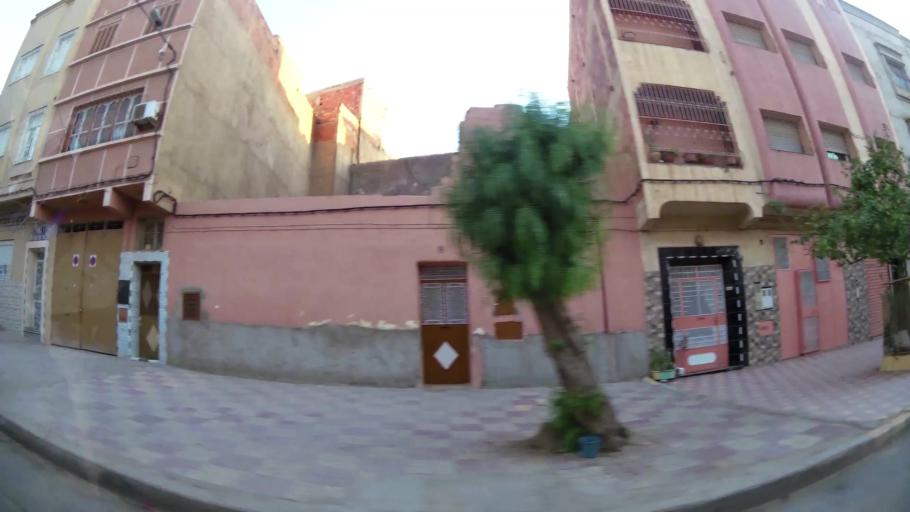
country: MA
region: Oriental
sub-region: Berkane-Taourirt
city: Berkane
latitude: 34.9192
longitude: -2.3288
